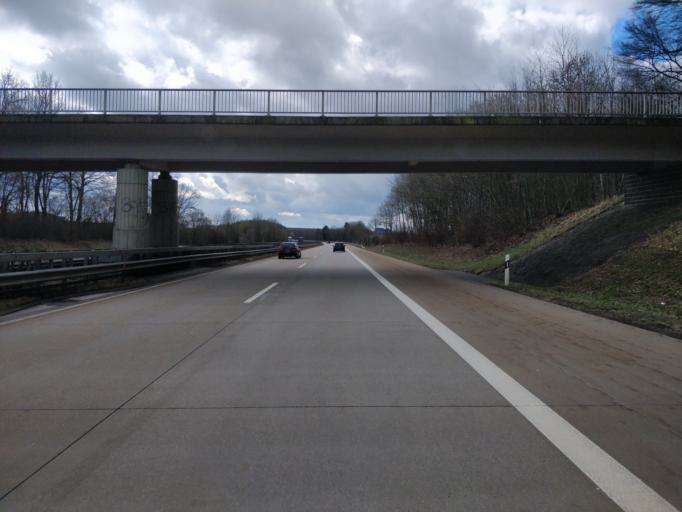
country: DE
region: Rheinland-Pfalz
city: Eckfeld
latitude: 50.1205
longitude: 6.8538
